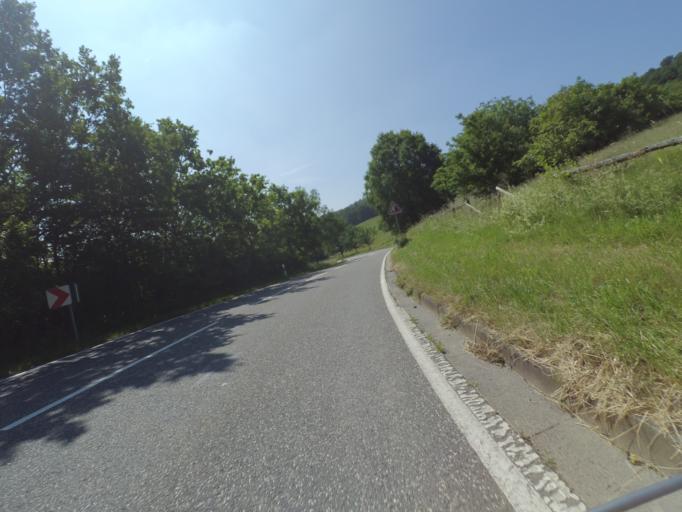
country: DE
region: Rheinland-Pfalz
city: Boppard
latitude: 50.2260
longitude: 7.5743
